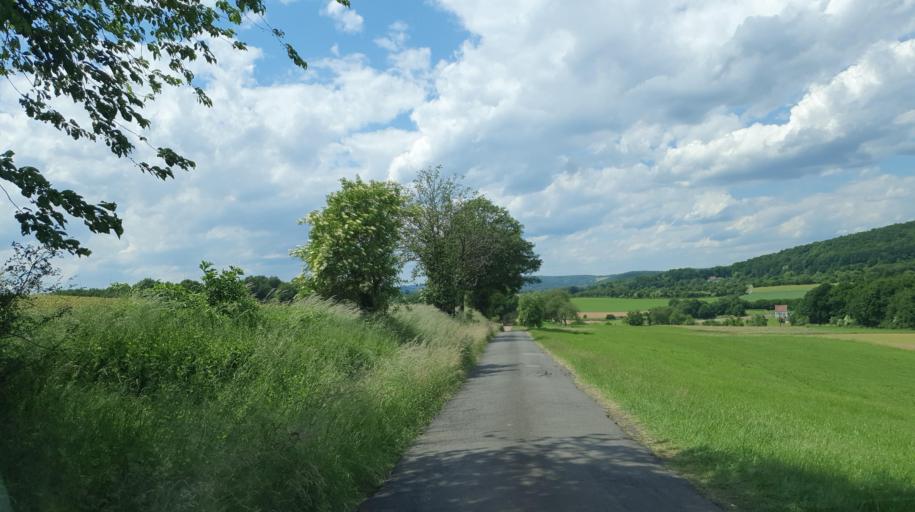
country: DE
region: Saarland
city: Sankt Wendel
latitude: 49.5076
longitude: 7.1802
